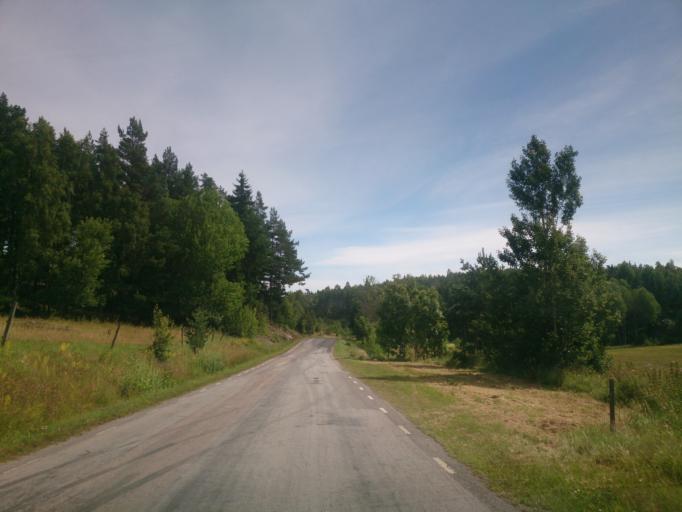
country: SE
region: OEstergoetland
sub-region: Valdemarsviks Kommun
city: Gusum
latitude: 58.3127
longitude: 16.5552
